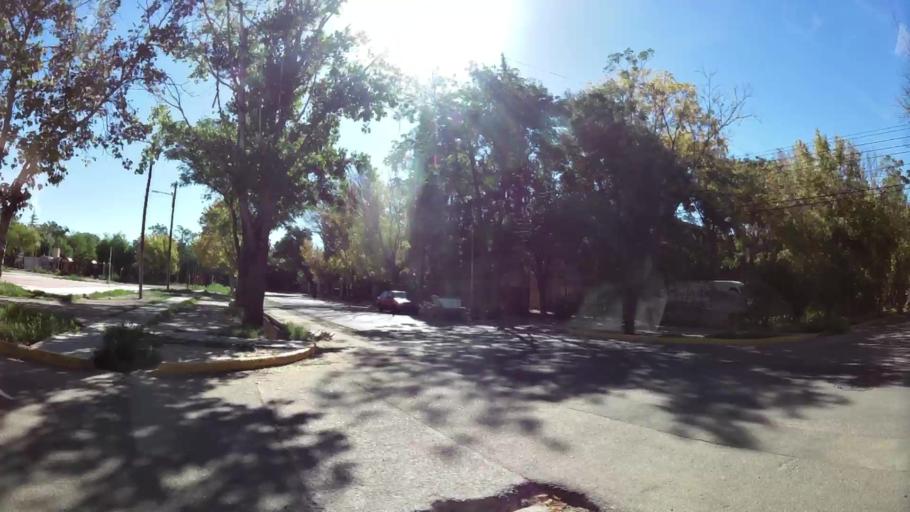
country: AR
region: Mendoza
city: Las Heras
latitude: -32.8445
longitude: -68.8212
